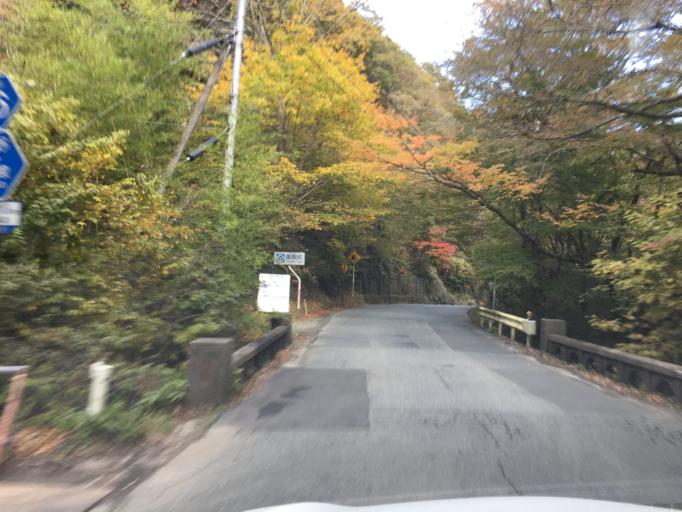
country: JP
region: Fukushima
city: Namie
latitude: 37.3516
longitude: 140.9074
